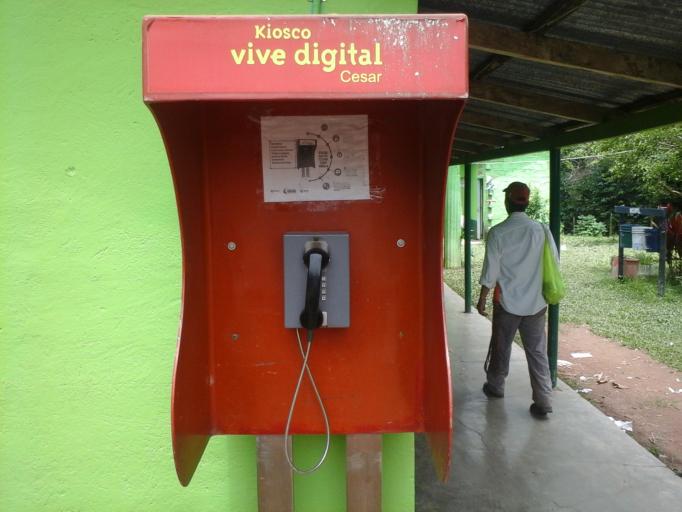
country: CO
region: Cesar
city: Agustin Codazzi
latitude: 9.9625
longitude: -73.0625
